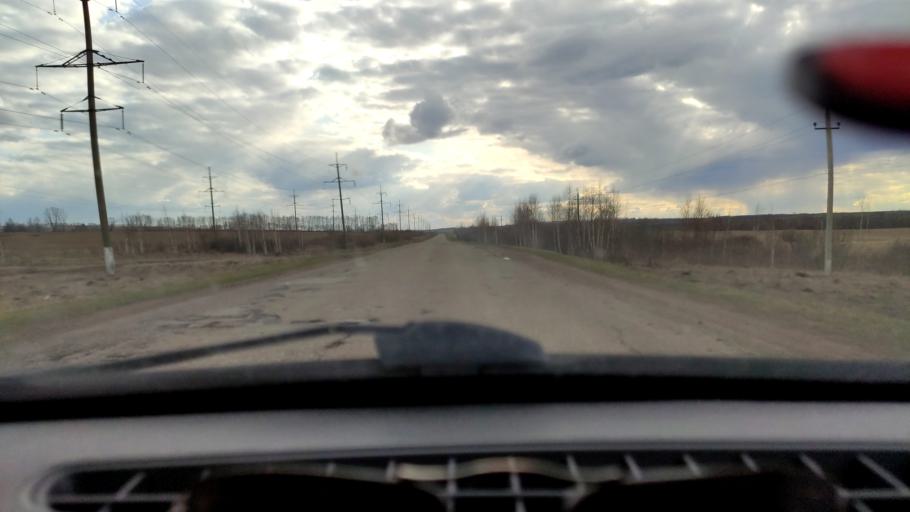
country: RU
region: Bashkortostan
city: Ulukulevo
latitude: 54.4211
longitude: 56.2860
